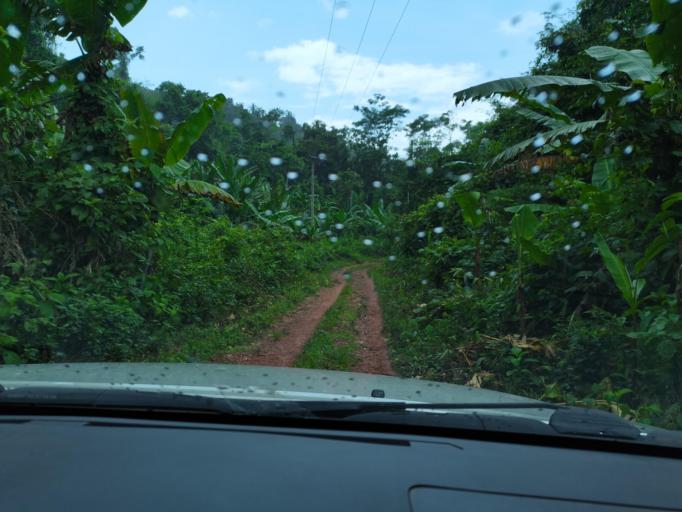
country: LA
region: Loungnamtha
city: Muang Nale
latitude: 20.5174
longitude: 101.0706
